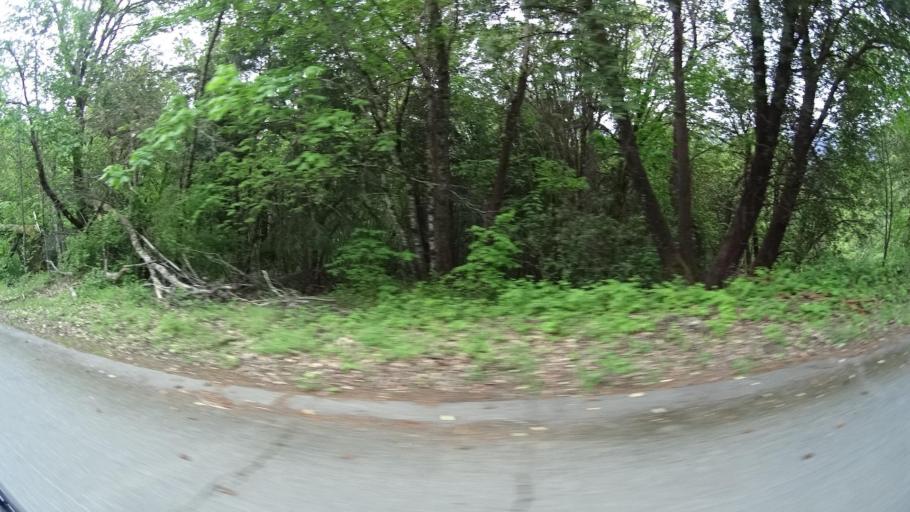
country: US
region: California
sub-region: Humboldt County
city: Willow Creek
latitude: 41.1178
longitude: -123.7220
